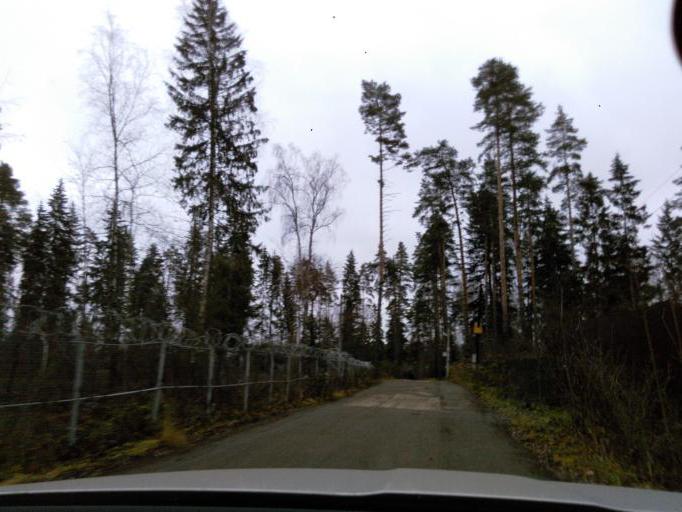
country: RU
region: Moskovskaya
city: Lozhki
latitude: 56.0529
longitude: 37.1000
